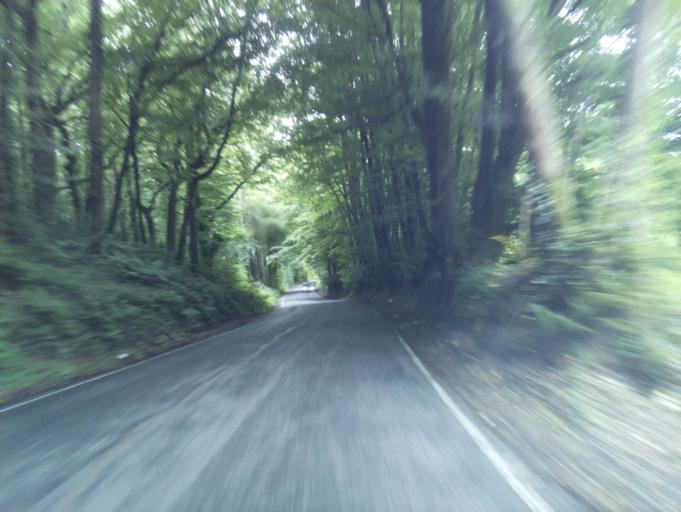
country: GB
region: England
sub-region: Devon
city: Ottery St Mary
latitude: 50.7547
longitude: -3.2366
